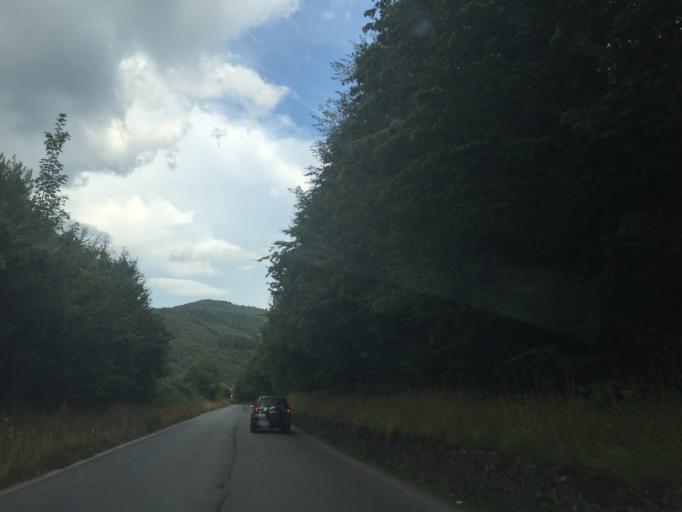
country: IT
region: Tuscany
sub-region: Provincia di Pistoia
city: Campo Tizzoro
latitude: 44.0379
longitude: 10.8764
